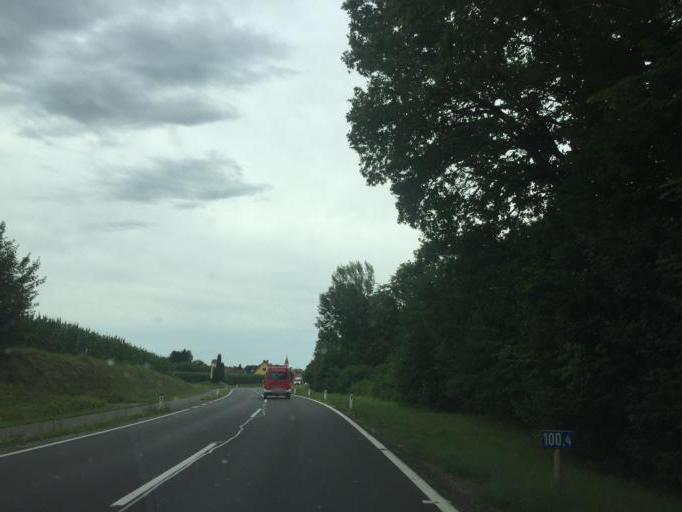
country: AT
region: Styria
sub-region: Politischer Bezirk Suedoststeiermark
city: Halbenrain
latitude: 46.7245
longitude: 15.9364
